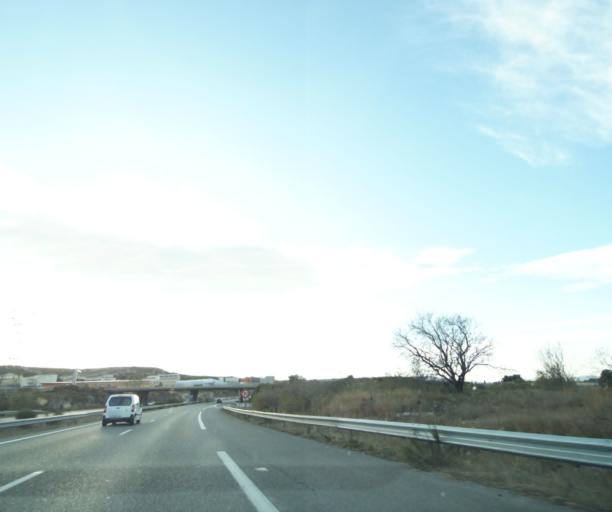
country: FR
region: Provence-Alpes-Cote d'Azur
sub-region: Departement des Bouches-du-Rhone
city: Gignac-la-Nerthe
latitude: 43.3812
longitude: 5.2248
